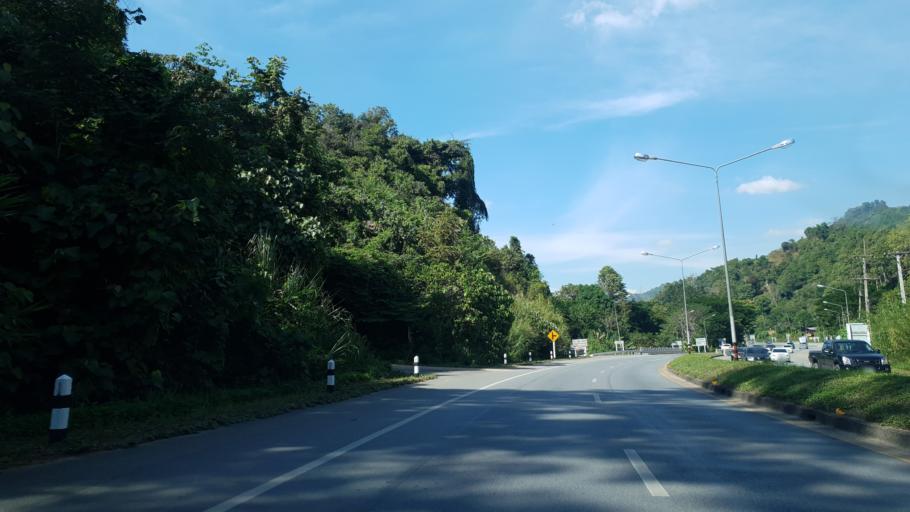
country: TH
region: Uttaradit
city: Lap Lae
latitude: 17.8063
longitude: 100.1090
